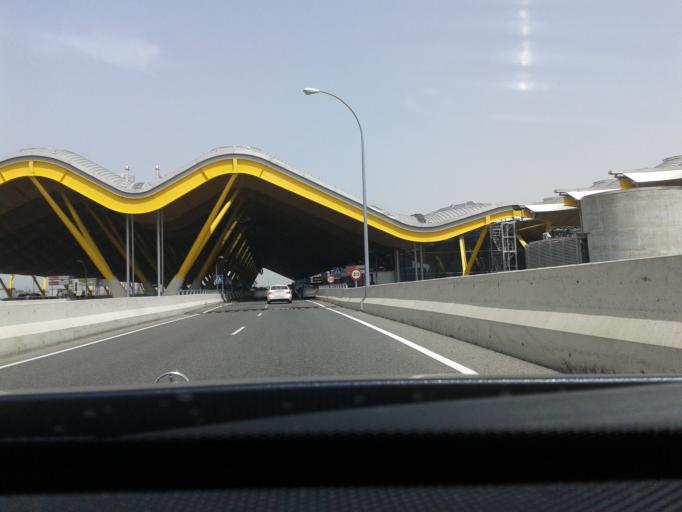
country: ES
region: Madrid
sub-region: Provincia de Madrid
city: Barajas de Madrid
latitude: 40.4896
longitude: -3.5932
